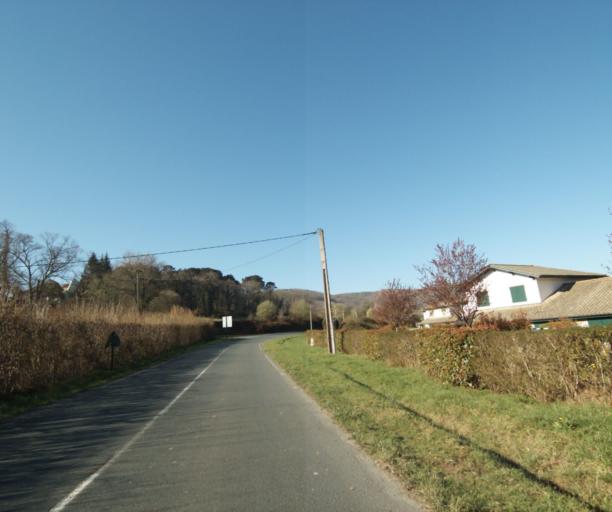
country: FR
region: Aquitaine
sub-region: Departement des Pyrenees-Atlantiques
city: Urrugne
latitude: 43.3350
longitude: -1.6686
